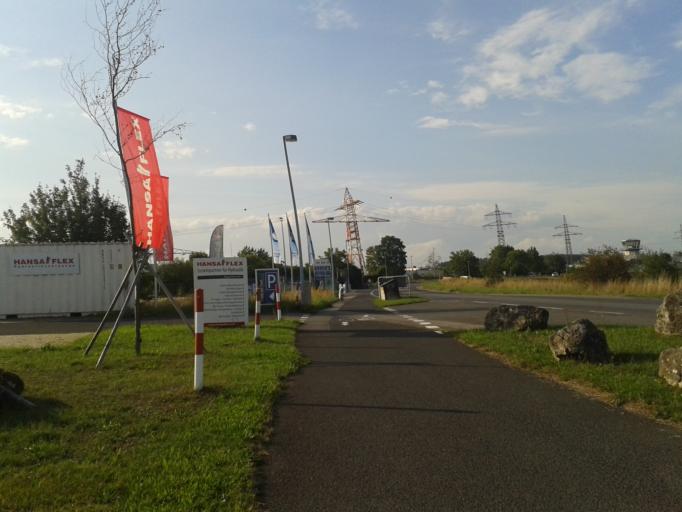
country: DE
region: Bavaria
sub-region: Upper Franconia
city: Bamberg
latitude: 49.9159
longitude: 10.9070
